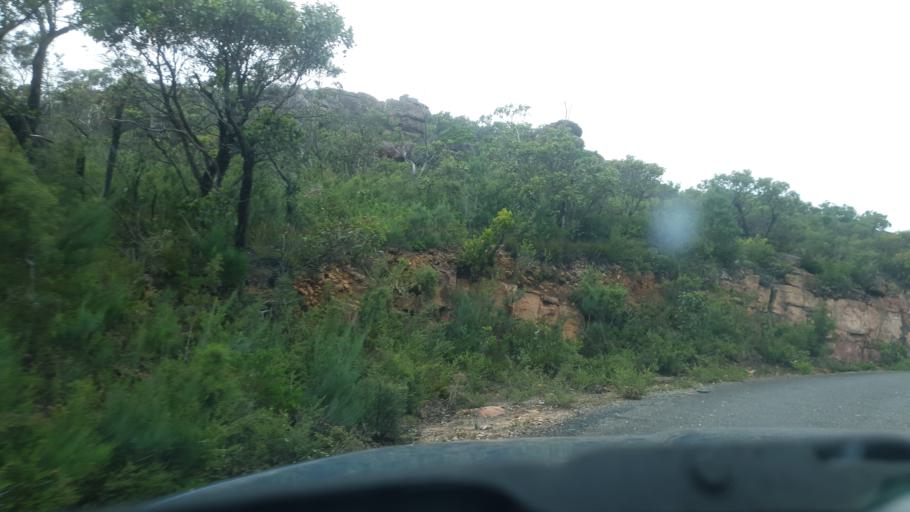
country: AU
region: Victoria
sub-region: Northern Grampians
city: Stawell
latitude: -37.2719
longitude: 142.5818
